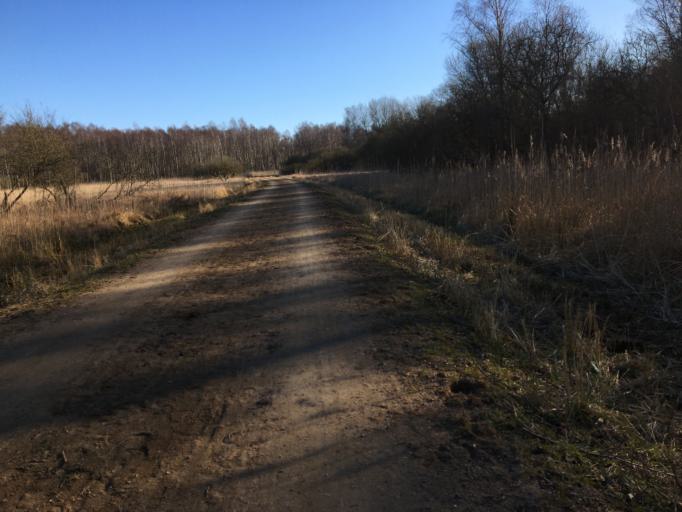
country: DK
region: Capital Region
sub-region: Tarnby Kommune
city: Tarnby
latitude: 55.5924
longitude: 12.5565
